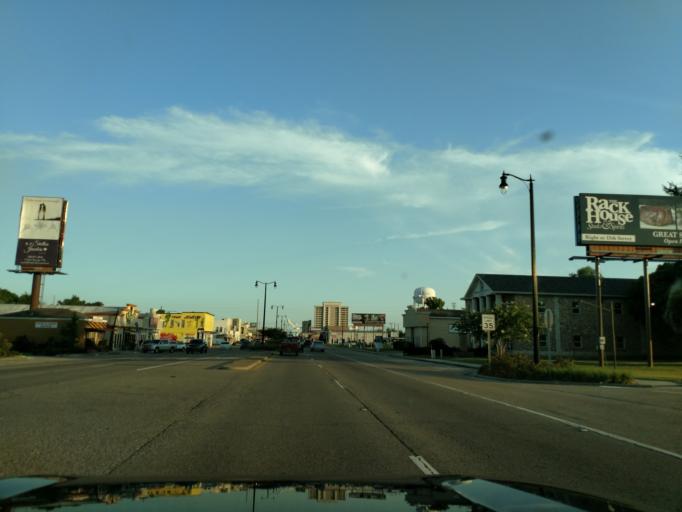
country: US
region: Mississippi
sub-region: Harrison County
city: Gulfport
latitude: 30.3768
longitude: -89.0931
